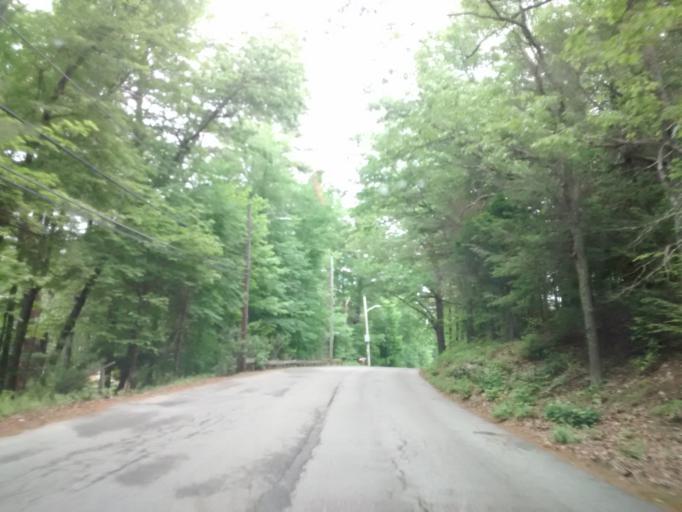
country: US
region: Rhode Island
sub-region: Providence County
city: Harrisville
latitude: 41.9718
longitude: -71.6723
